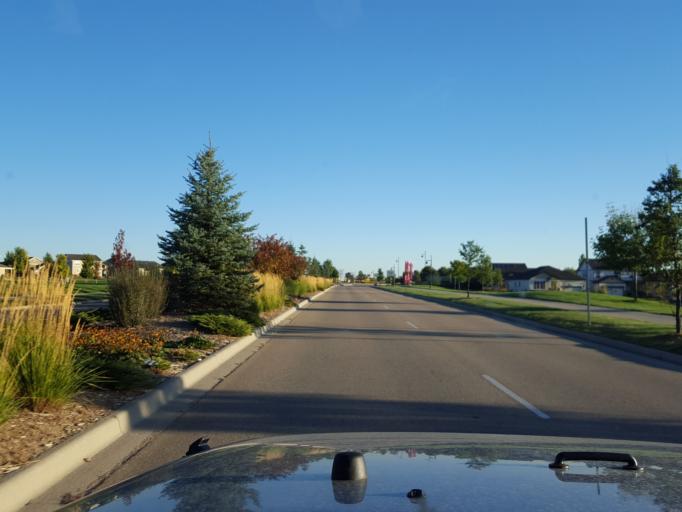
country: US
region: Colorado
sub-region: Weld County
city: Dacono
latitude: 40.0906
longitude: -104.9988
